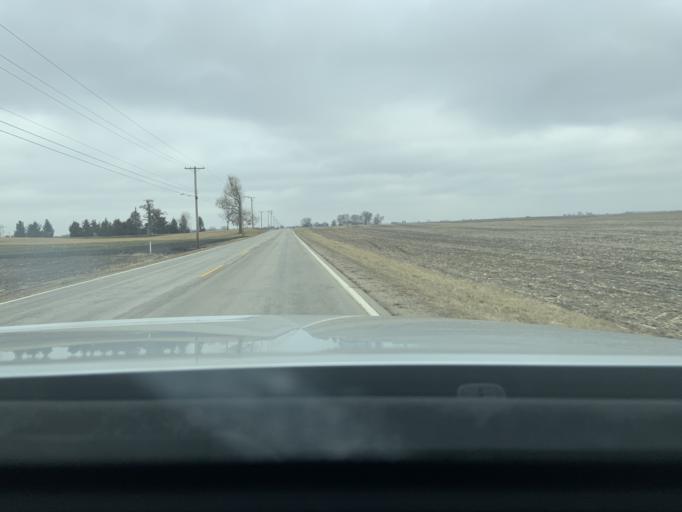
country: US
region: Illinois
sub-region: LaSalle County
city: Seneca
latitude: 41.3425
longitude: -88.6115
